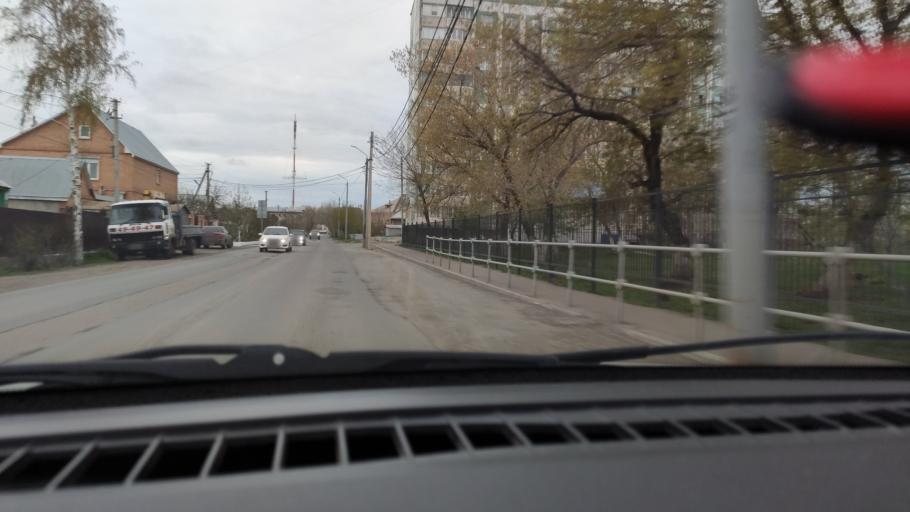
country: RU
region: Orenburg
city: Orenburg
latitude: 51.7769
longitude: 55.1289
